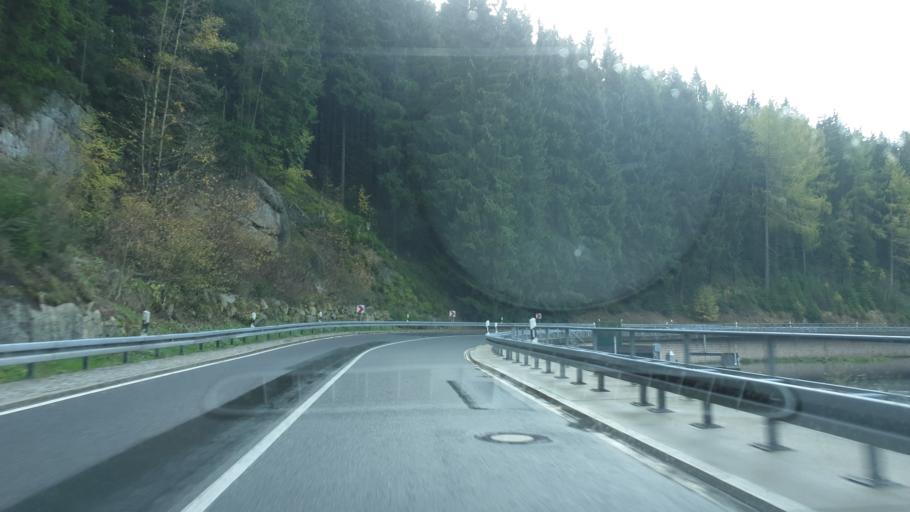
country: DE
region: Saxony
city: Schoenheide
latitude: 50.4816
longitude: 12.5334
